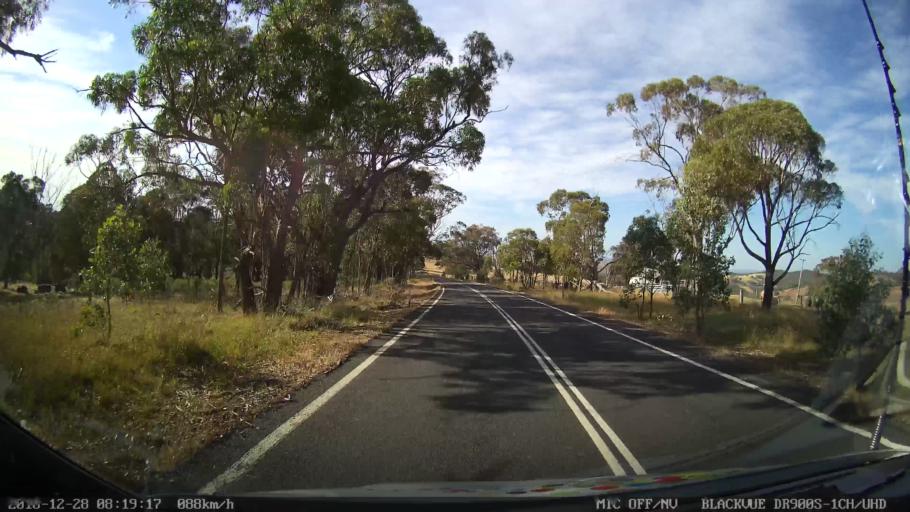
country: AU
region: New South Wales
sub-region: Blayney
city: Blayney
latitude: -33.8570
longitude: 149.3507
